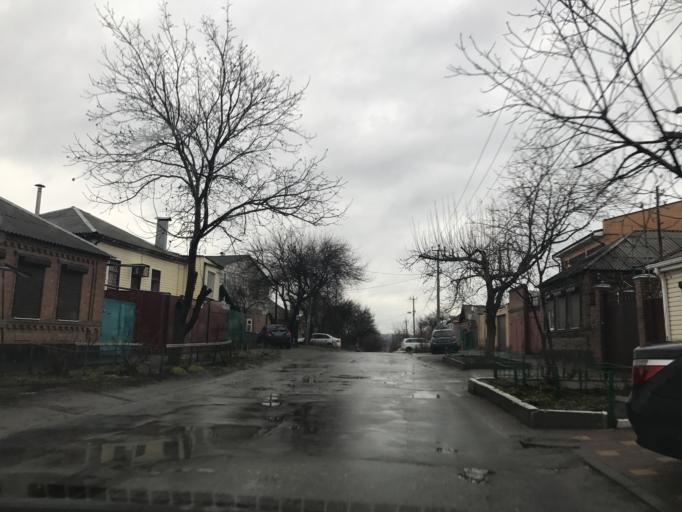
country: RU
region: Rostov
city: Rostov-na-Donu
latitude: 47.2342
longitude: 39.6770
